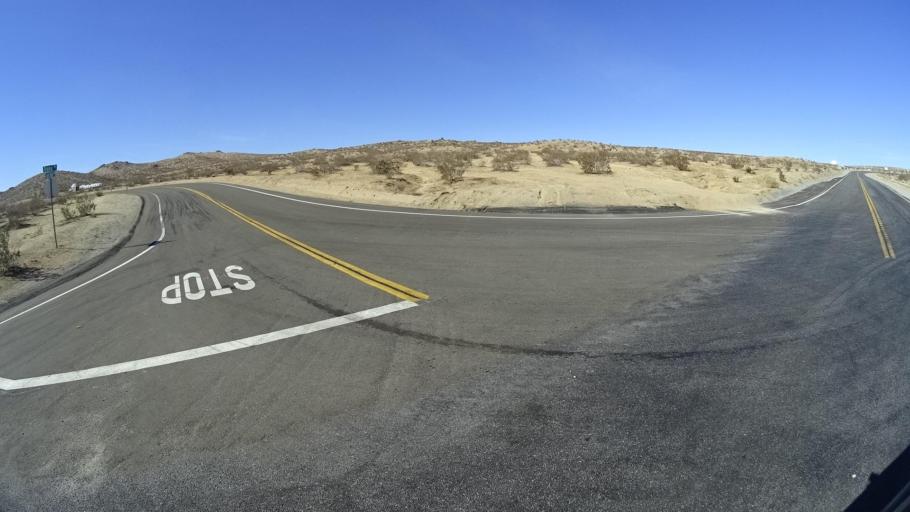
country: US
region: California
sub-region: Kern County
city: Ridgecrest
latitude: 35.5409
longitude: -117.5805
